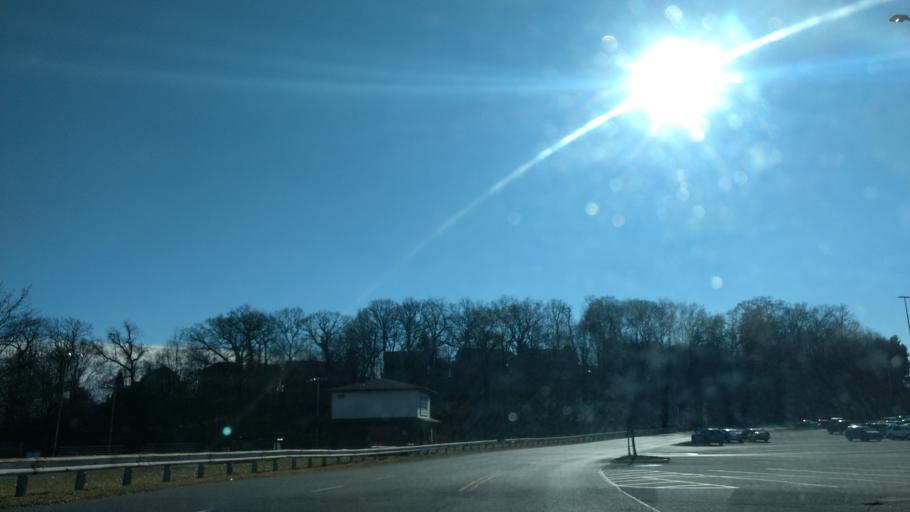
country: US
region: Pennsylvania
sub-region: Allegheny County
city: West View
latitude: 40.5448
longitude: -80.0046
